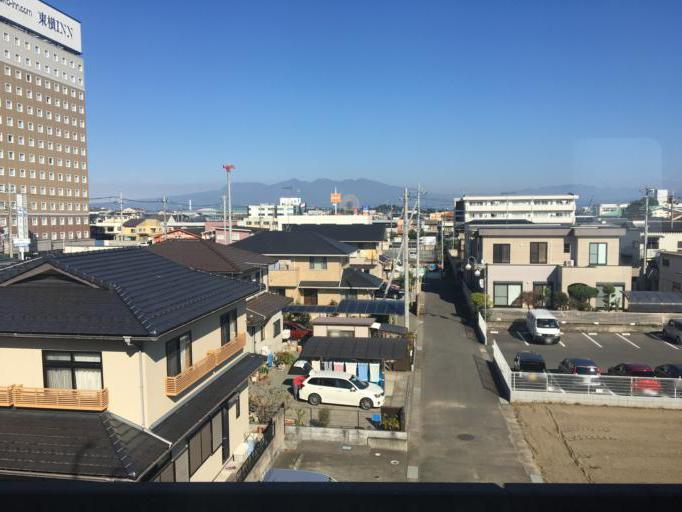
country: JP
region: Gunma
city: Isesaki
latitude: 36.3263
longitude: 139.1988
